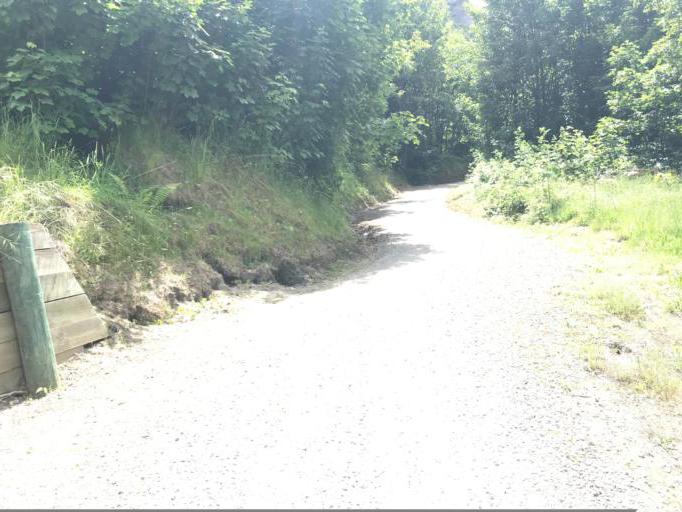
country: NZ
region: Otago
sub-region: Queenstown-Lakes District
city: Arrowtown
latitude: -45.0092
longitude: 168.8954
